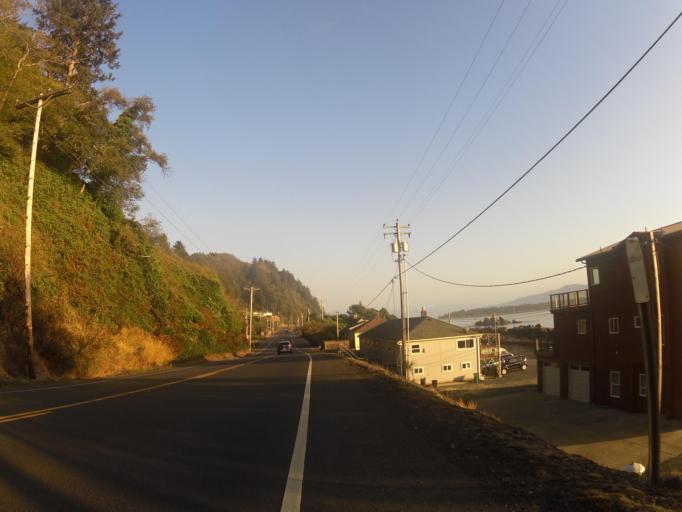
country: US
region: Oregon
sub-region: Tillamook County
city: Rockaway Beach
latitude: 45.5674
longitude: -123.9406
